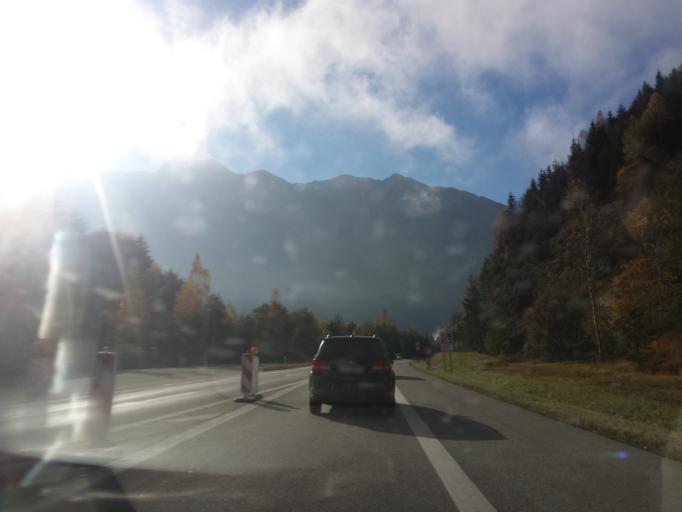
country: DE
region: Bavaria
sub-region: Upper Bavaria
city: Eschenlohe
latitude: 47.5912
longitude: 11.1759
